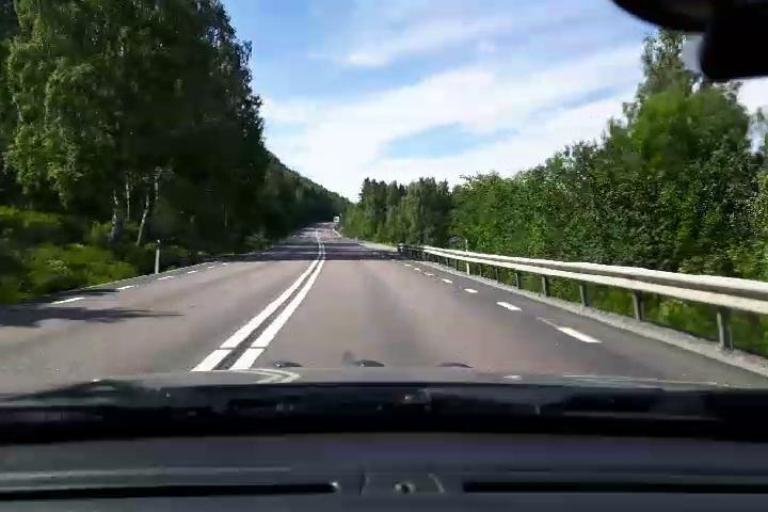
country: SE
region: Gaevleborg
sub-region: Bollnas Kommun
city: Kilafors
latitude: 61.1917
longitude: 16.7712
